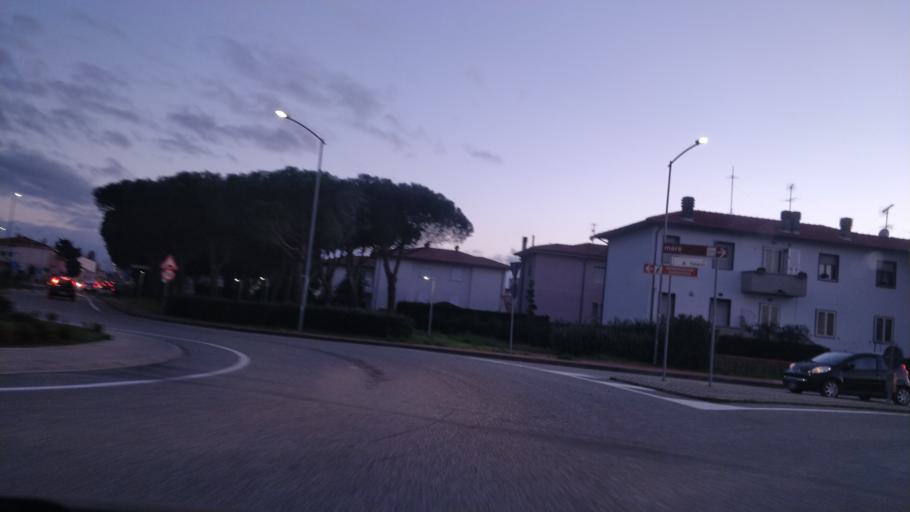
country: IT
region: Tuscany
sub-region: Provincia di Livorno
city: Vada
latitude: 43.3552
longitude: 10.4553
